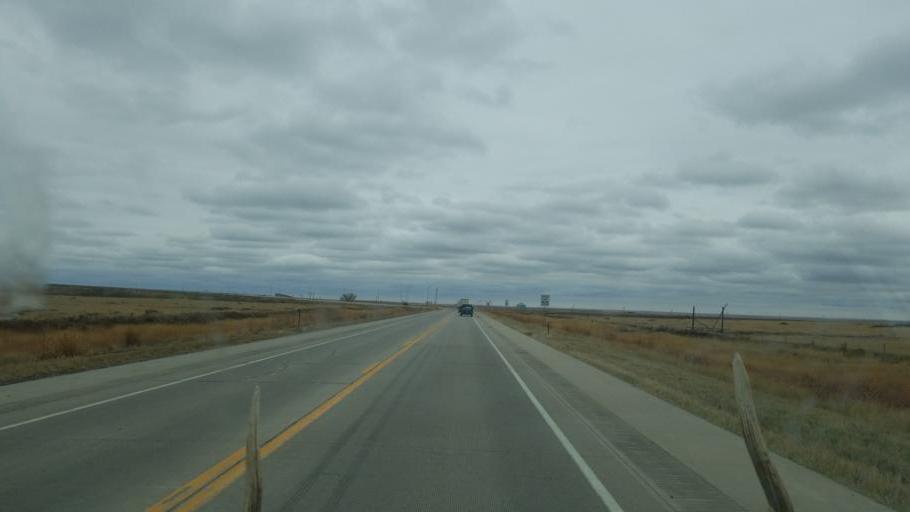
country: US
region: Colorado
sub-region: Kiowa County
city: Eads
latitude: 38.7562
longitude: -102.7768
